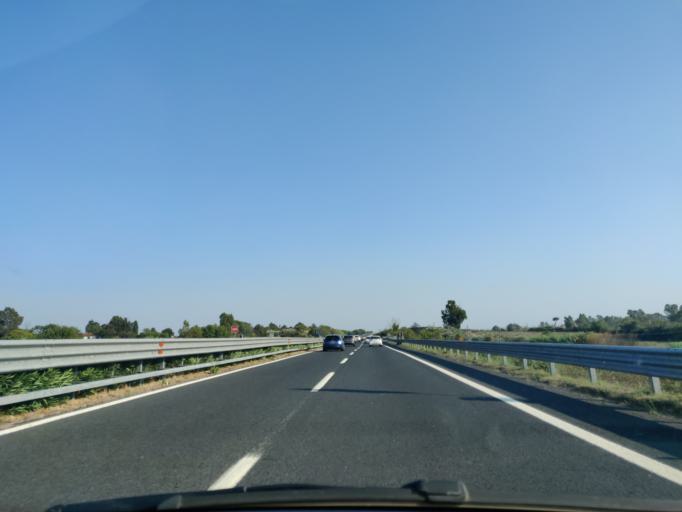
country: IT
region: Latium
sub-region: Citta metropolitana di Roma Capitale
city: Npp 23 (Parco Leonardo)
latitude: 41.8375
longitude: 12.2818
